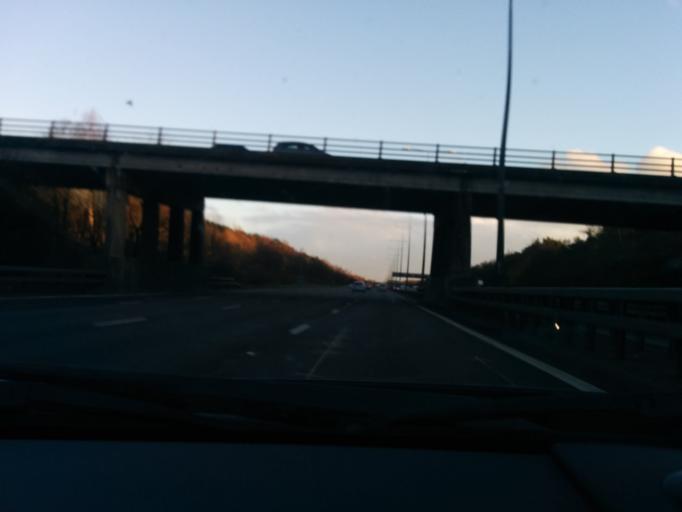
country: GB
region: England
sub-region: Buckinghamshire
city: Beaconsfield
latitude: 51.5944
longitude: -0.6276
